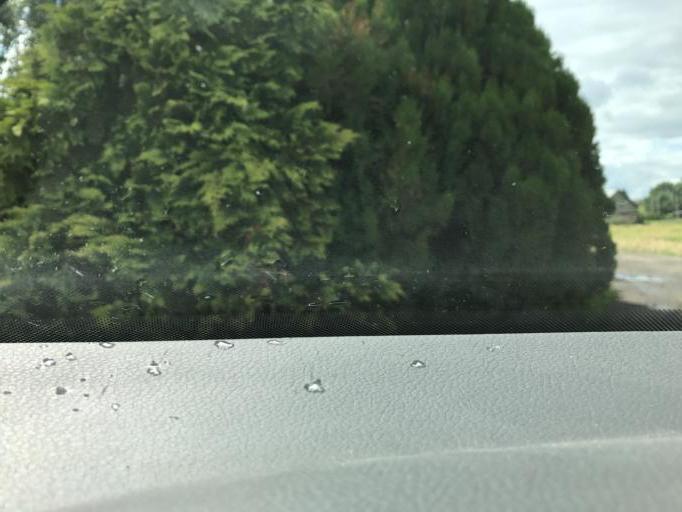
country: PL
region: Pomeranian Voivodeship
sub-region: Powiat gdanski
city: Pruszcz Gdanski
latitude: 54.2612
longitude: 18.6809
